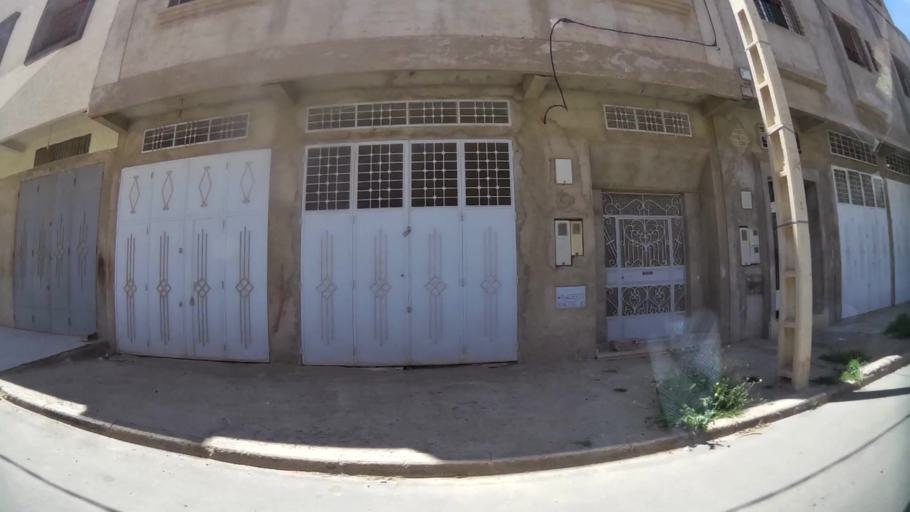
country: MA
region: Oriental
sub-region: Oujda-Angad
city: Oujda
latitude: 34.6622
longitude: -1.9501
